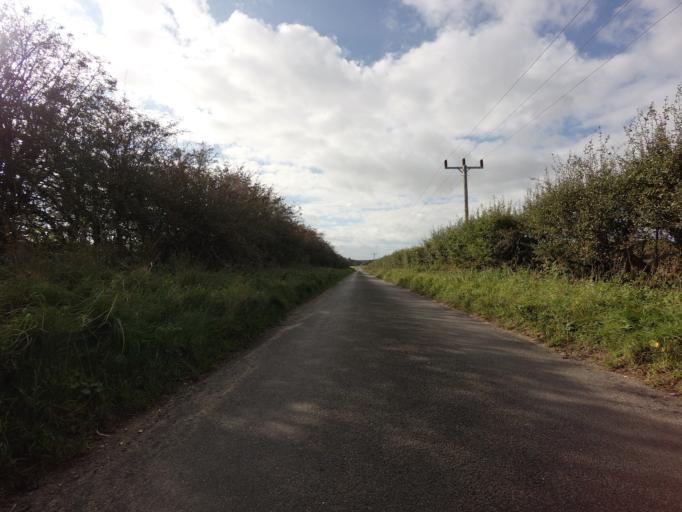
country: GB
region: England
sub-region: Norfolk
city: Hunstanton
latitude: 52.9352
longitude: 0.5757
